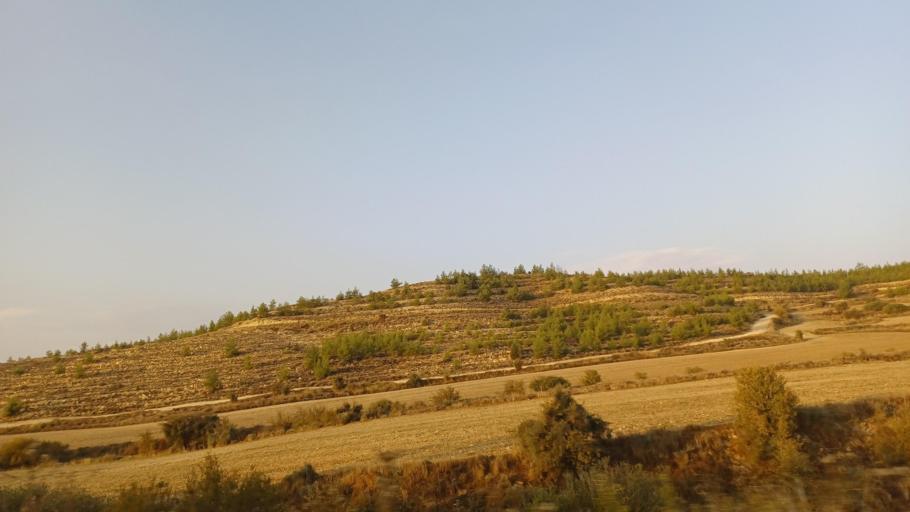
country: CY
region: Larnaka
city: Athienou
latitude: 35.0026
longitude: 33.5251
